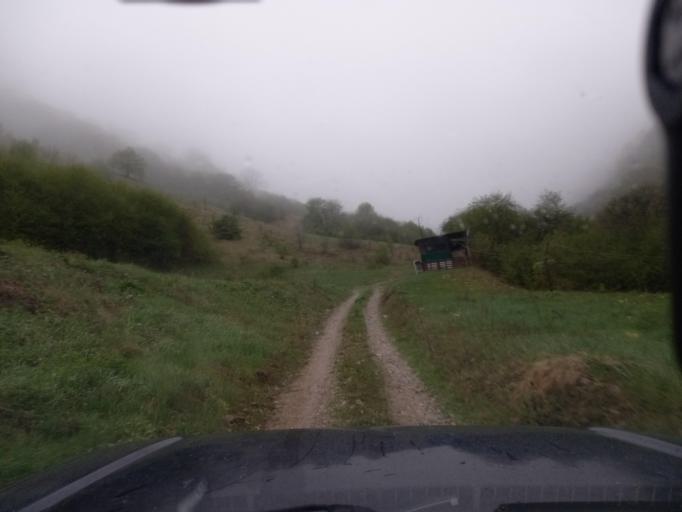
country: RU
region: Kabardino-Balkariya
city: Zhankhoteko
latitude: 43.4927
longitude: 43.1555
